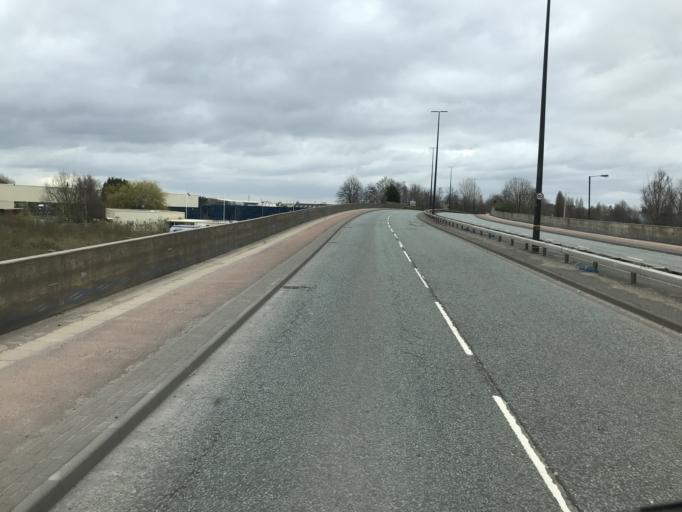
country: GB
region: England
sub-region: City and Borough of Salford
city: Eccles
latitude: 53.4789
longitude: -2.3249
